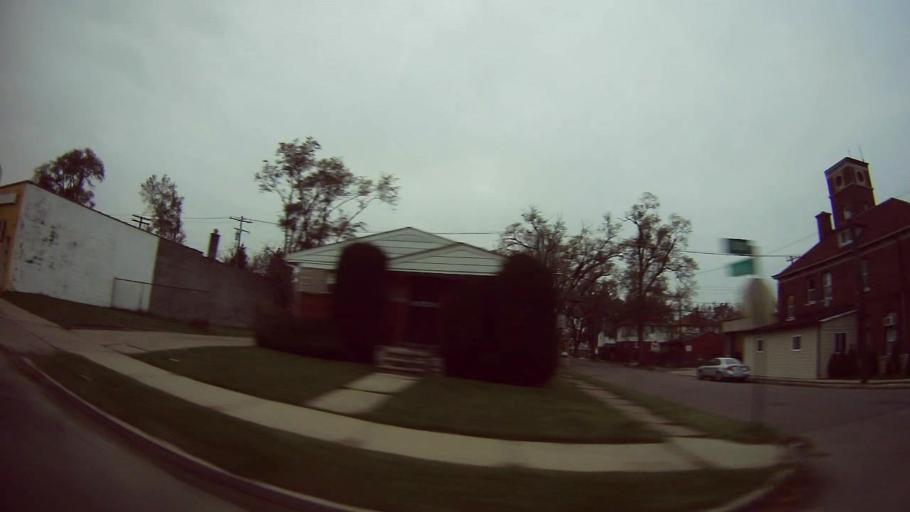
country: US
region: Michigan
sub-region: Wayne County
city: Hamtramck
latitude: 42.4297
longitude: -83.0629
